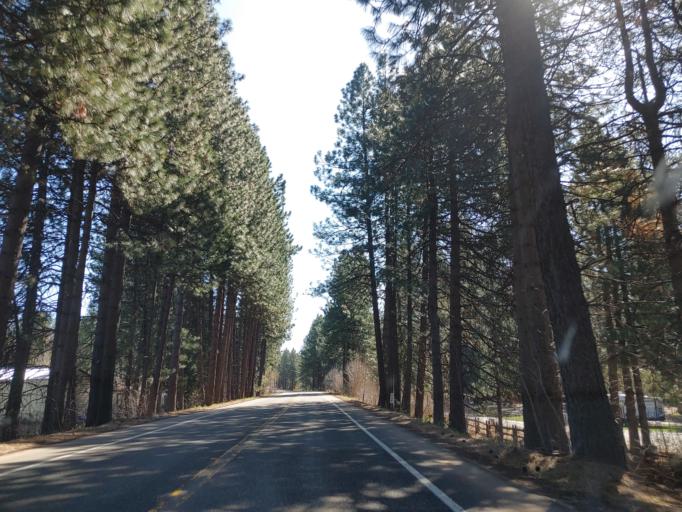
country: US
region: California
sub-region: Siskiyou County
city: McCloud
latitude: 41.2510
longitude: -122.1327
